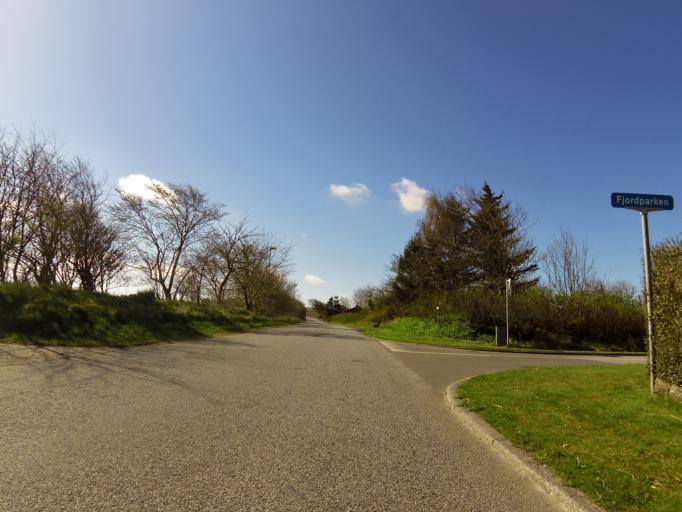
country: DK
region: Central Jutland
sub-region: Holstebro Kommune
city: Vinderup
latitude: 56.4691
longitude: 8.7219
